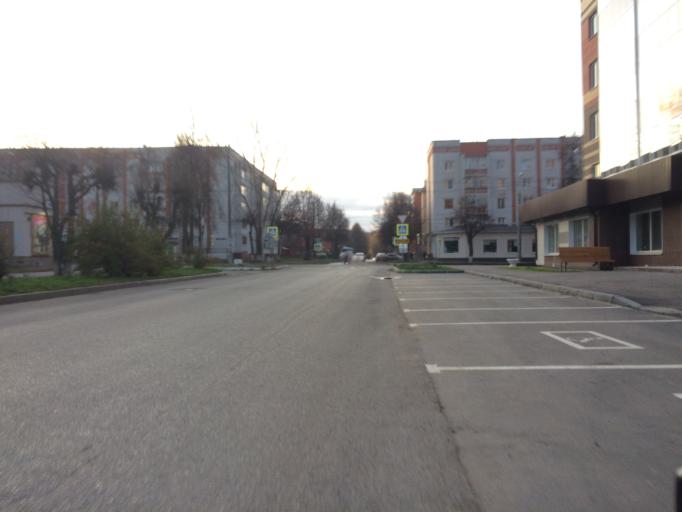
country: RU
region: Mariy-El
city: Yoshkar-Ola
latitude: 56.6478
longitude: 47.8945
